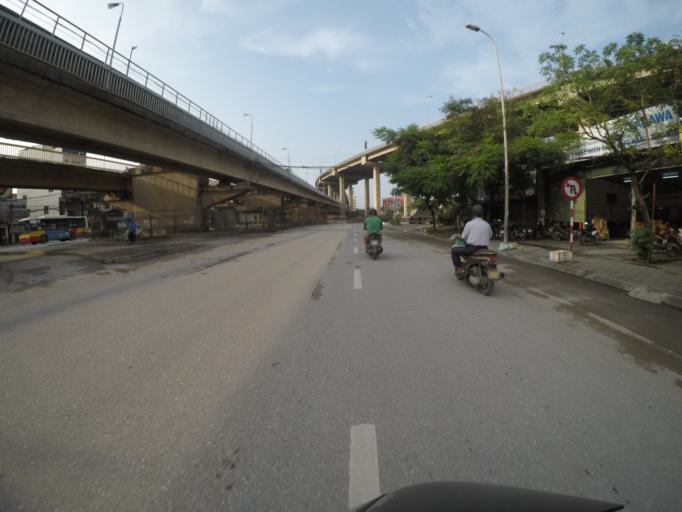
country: VN
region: Ha Noi
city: Tay Ho
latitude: 21.0882
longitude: 105.7859
